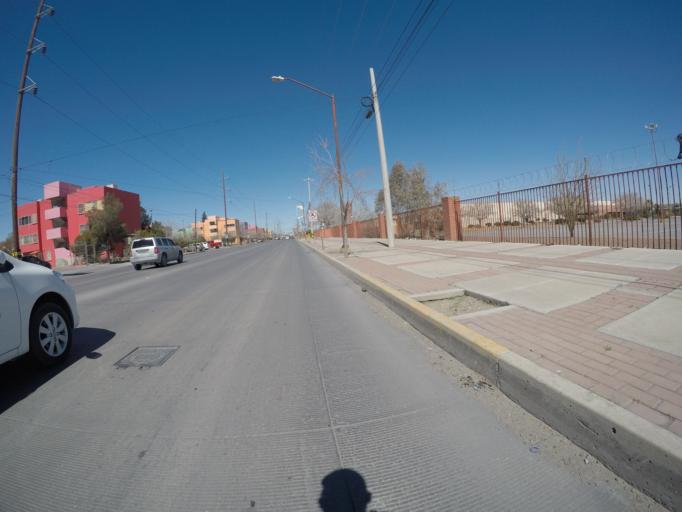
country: MX
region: Chihuahua
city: Ciudad Juarez
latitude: 31.7507
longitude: -106.4412
